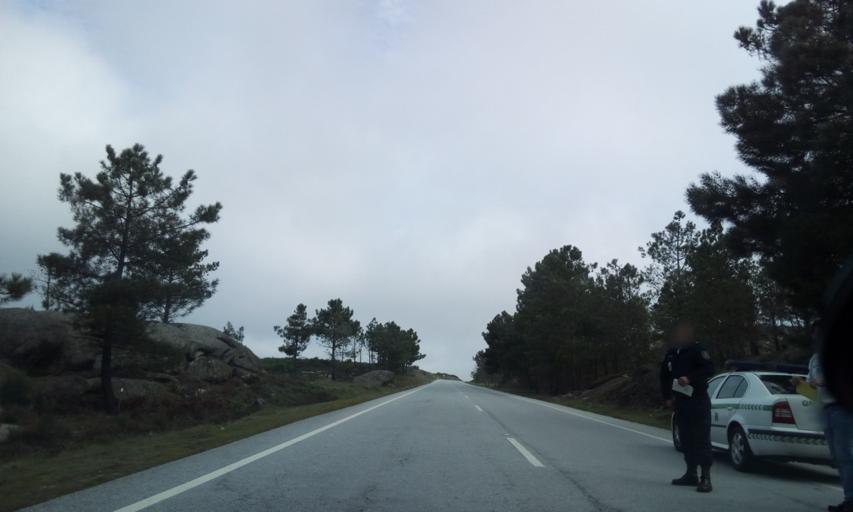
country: PT
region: Guarda
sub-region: Aguiar da Beira
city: Aguiar da Beira
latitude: 40.7587
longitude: -7.5026
